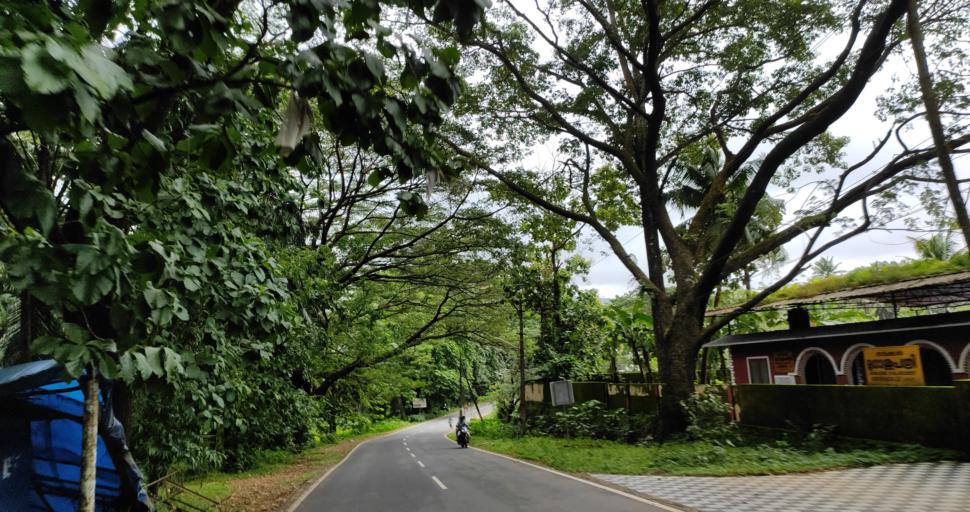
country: IN
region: Kerala
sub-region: Ernakulam
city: Angamali
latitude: 10.2949
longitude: 76.4838
